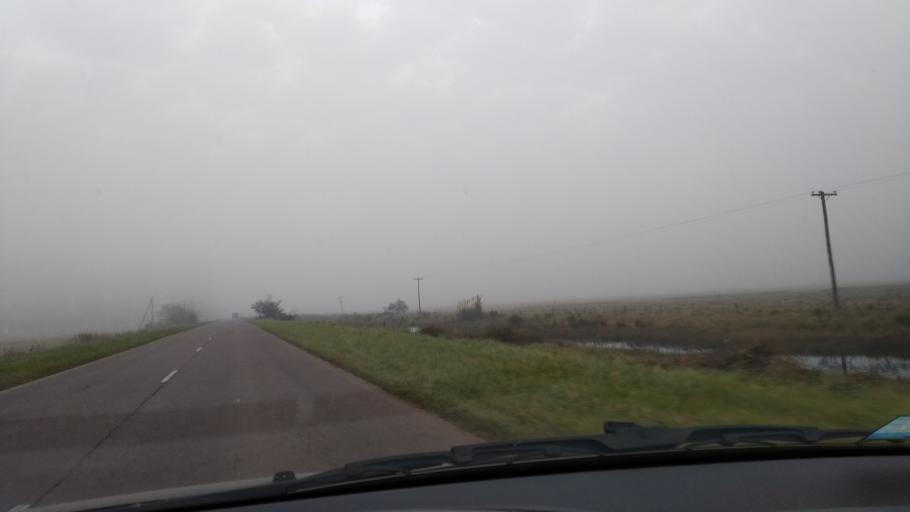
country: AR
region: Buenos Aires
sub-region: Partido de San Vicente
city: San Vicente
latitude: -35.2265
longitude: -58.4468
